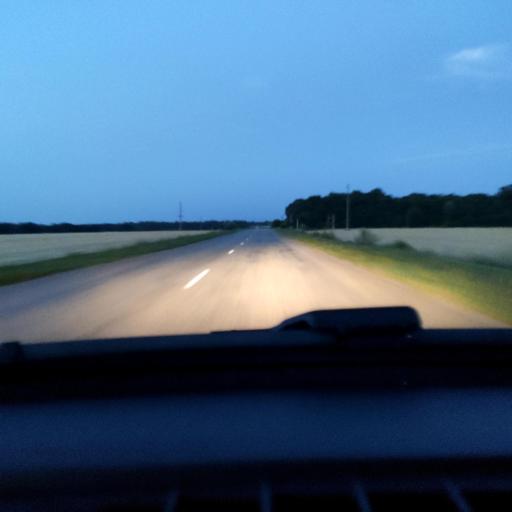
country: RU
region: Lipetsk
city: Zadonsk
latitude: 52.2973
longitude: 38.8208
